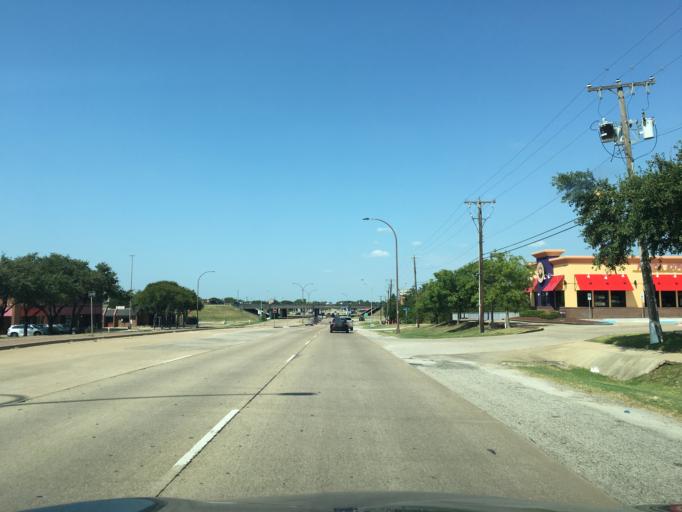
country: US
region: Texas
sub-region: Tarrant County
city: Kennedale
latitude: 32.6705
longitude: -97.2023
